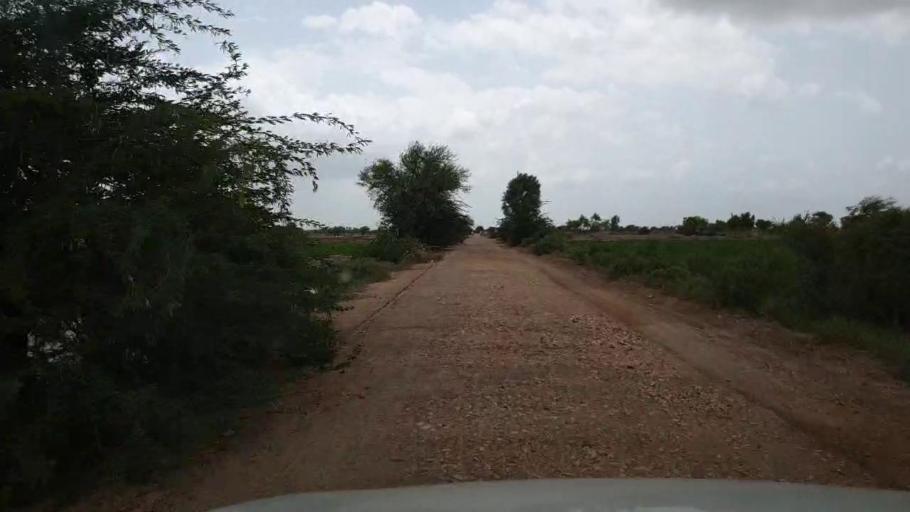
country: PK
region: Sindh
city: Kario
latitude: 24.7501
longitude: 68.4701
